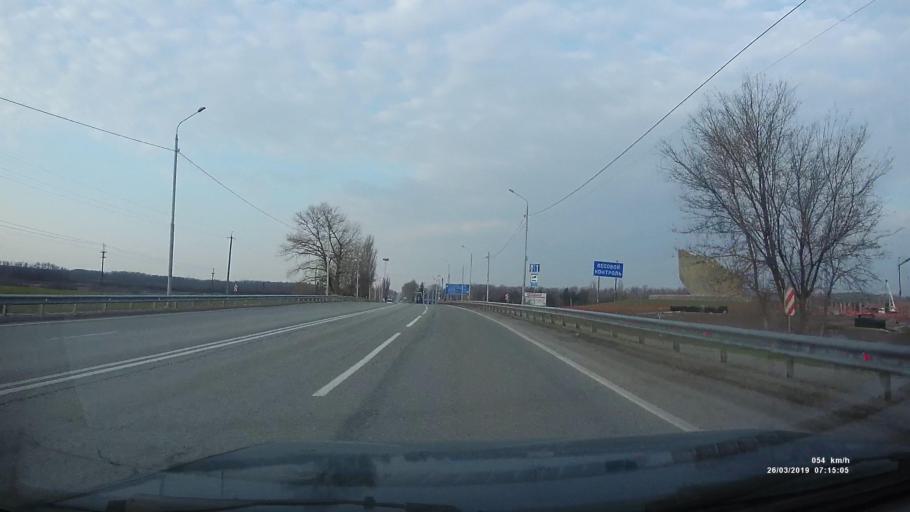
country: RU
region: Rostov
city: Primorka
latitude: 47.3171
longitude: 39.0133
